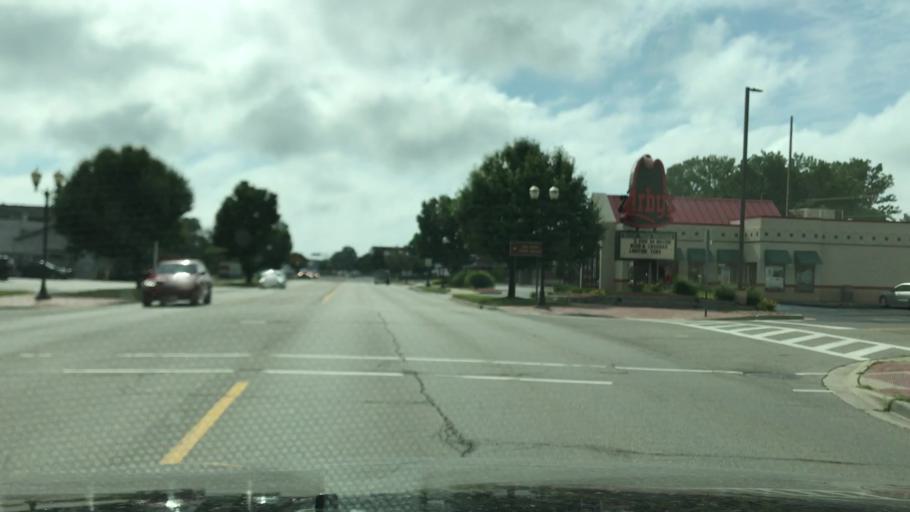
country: US
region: Michigan
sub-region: Ottawa County
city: Spring Lake
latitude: 43.0767
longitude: -86.2030
